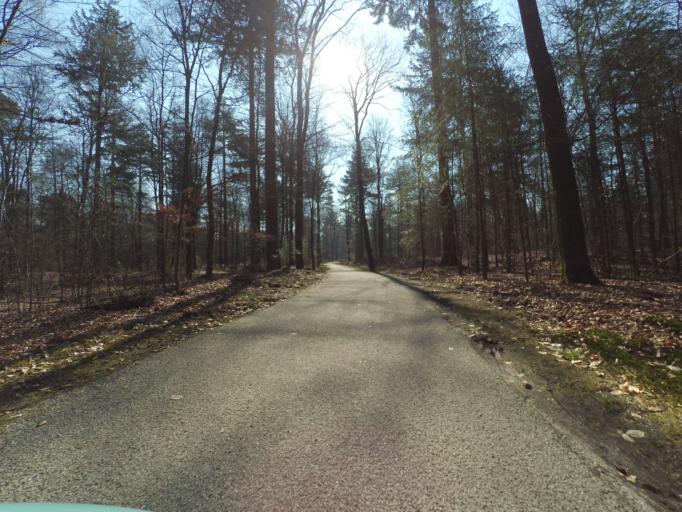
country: NL
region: Gelderland
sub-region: Gemeente Ede
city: Otterlo
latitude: 52.1217
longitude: 5.8349
